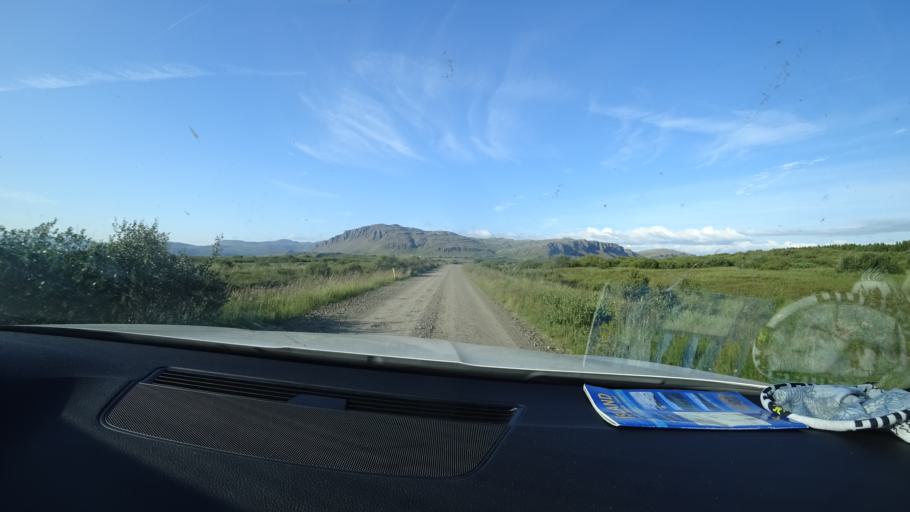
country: IS
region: West
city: Borgarnes
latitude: 64.6782
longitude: -21.9555
